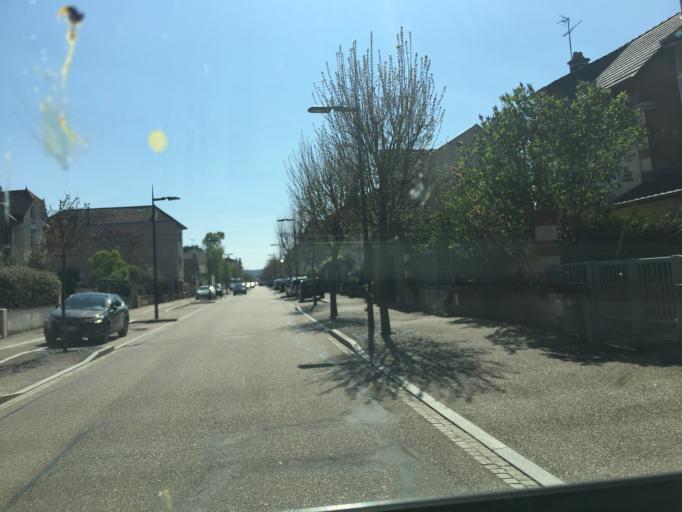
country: FR
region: Lorraine
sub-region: Departement de Meurthe-et-Moselle
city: Pont-a-Mousson
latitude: 48.9103
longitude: 6.0614
